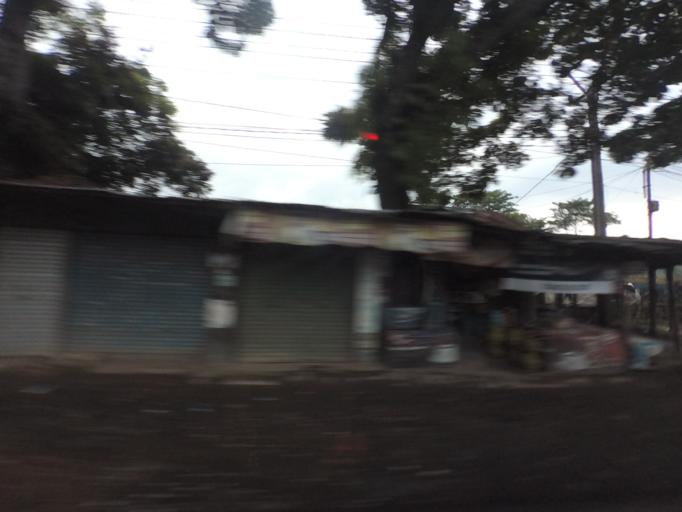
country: ID
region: West Java
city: Cicurug
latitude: -6.8396
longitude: 106.7612
